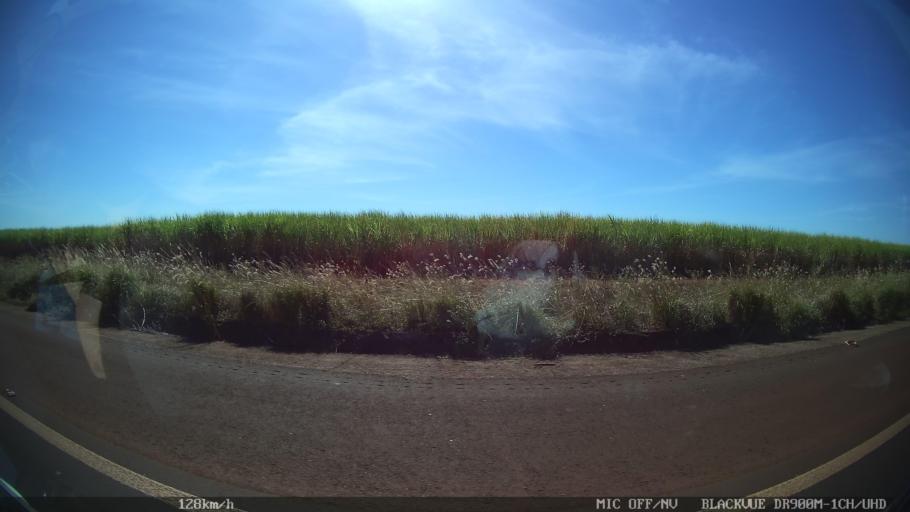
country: BR
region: Sao Paulo
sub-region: Guaira
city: Guaira
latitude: -20.4440
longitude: -48.3556
